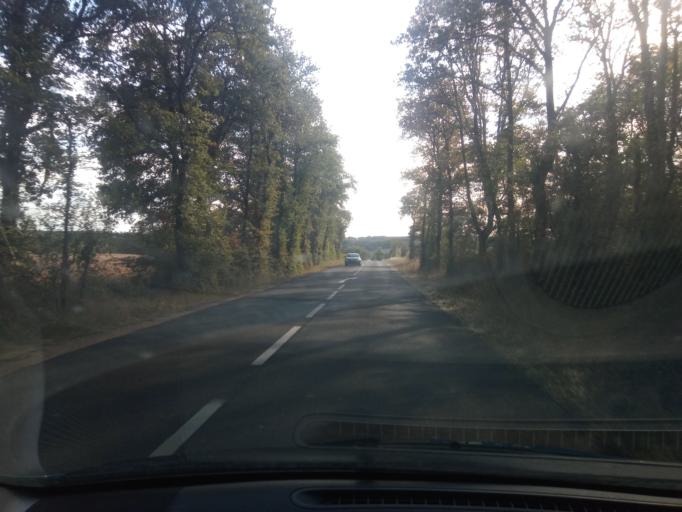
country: FR
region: Poitou-Charentes
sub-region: Departement de la Vienne
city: Montmorillon
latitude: 46.4976
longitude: 0.8433
